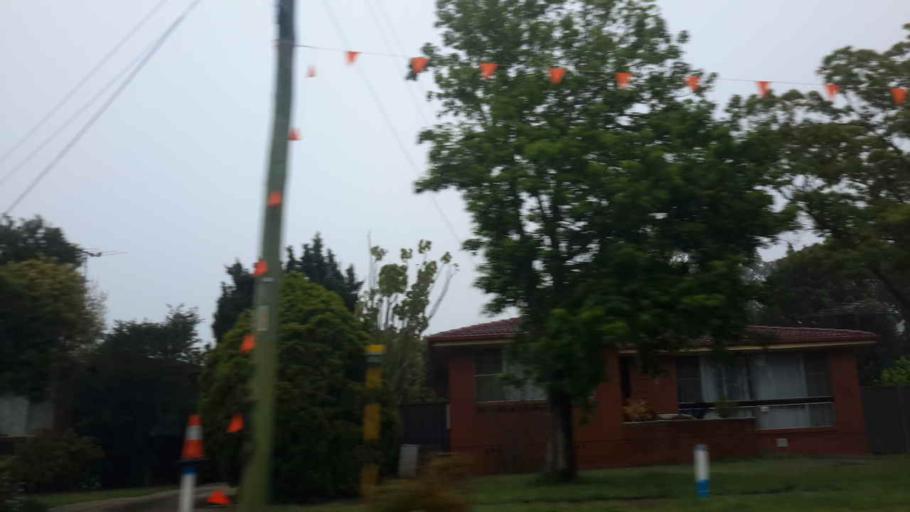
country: AU
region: New South Wales
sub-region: Penrith Municipality
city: Kingswood Park
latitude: -33.7730
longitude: 150.7115
